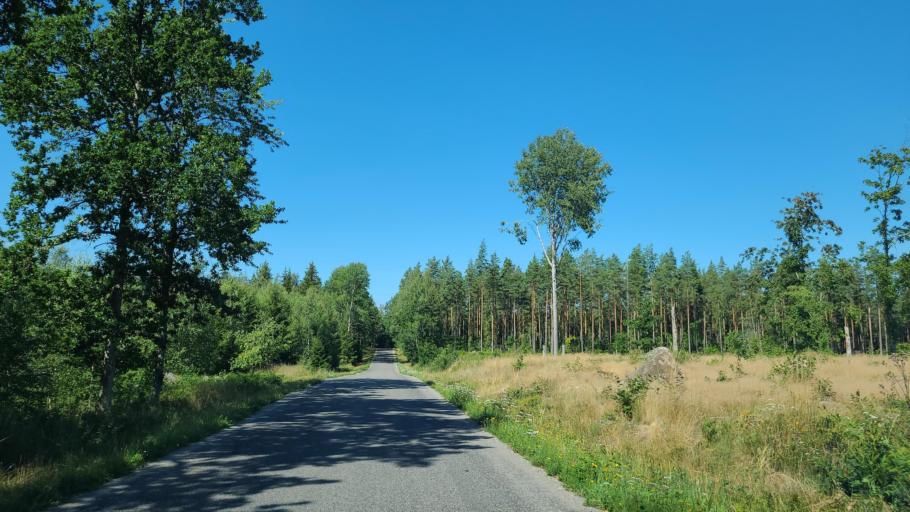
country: SE
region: Kalmar
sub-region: Kalmar Kommun
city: Ljungbyholm
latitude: 56.5699
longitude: 16.0492
